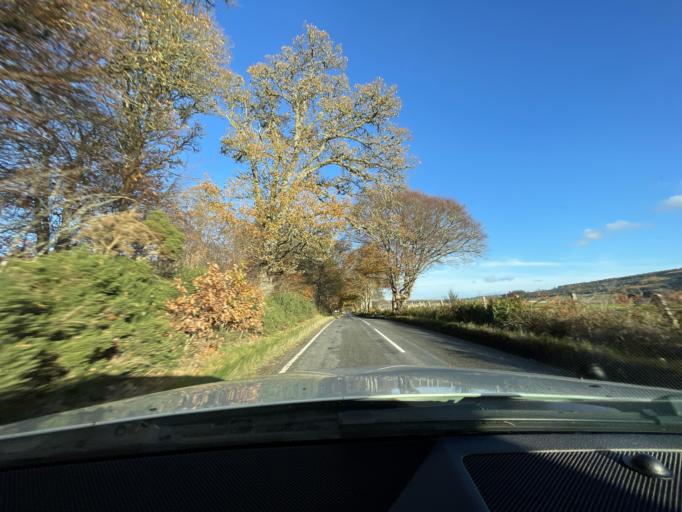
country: GB
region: Scotland
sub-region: Highland
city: Inverness
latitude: 57.4242
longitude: -4.2917
